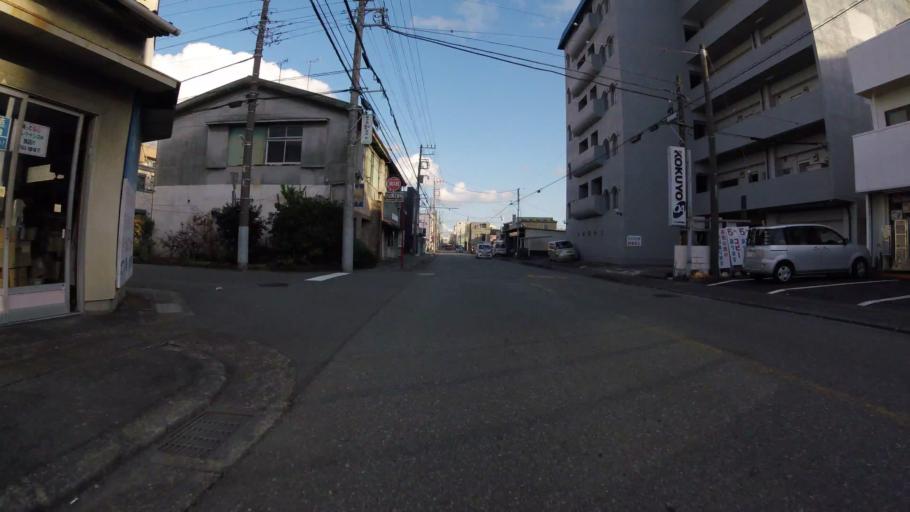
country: JP
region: Shizuoka
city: Fuji
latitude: 35.1544
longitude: 138.6463
